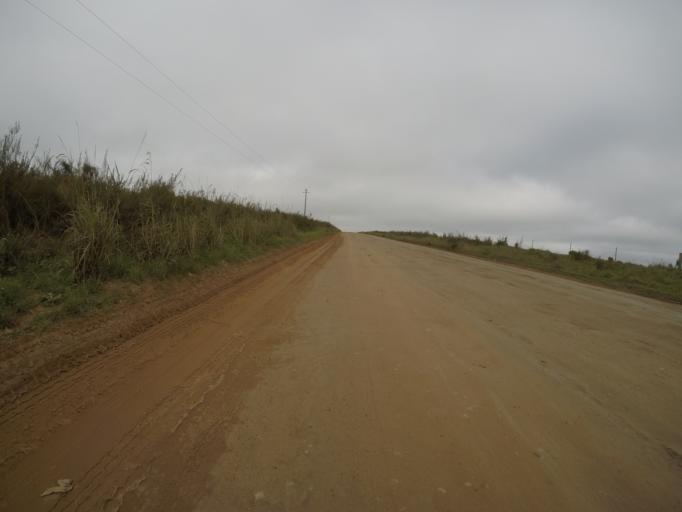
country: ZA
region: Eastern Cape
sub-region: Cacadu District Municipality
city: Kareedouw
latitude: -34.0205
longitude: 24.2398
